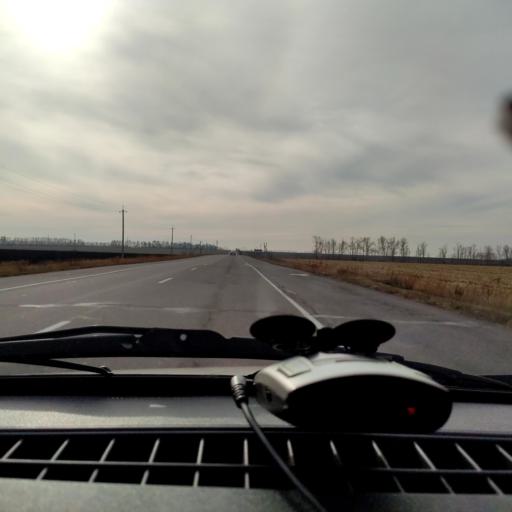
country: RU
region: Voronezj
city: Strelitsa
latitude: 51.5565
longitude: 38.9722
